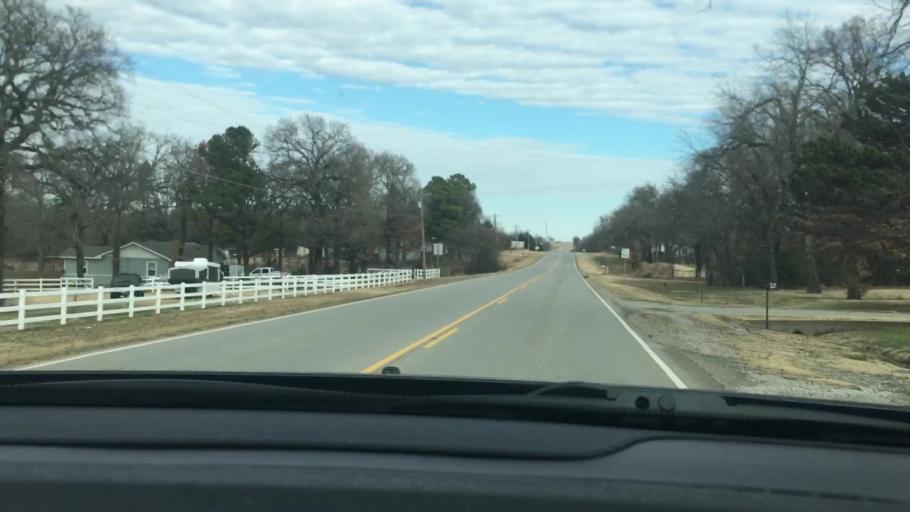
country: US
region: Oklahoma
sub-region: Garvin County
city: Pauls Valley
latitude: 34.7732
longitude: -97.1849
